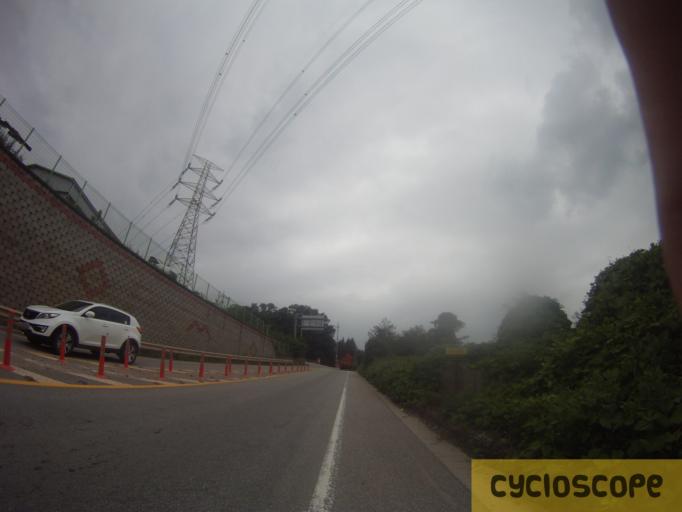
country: KR
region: Gyeonggi-do
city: Hwaseong-si
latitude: 37.1678
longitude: 126.9317
